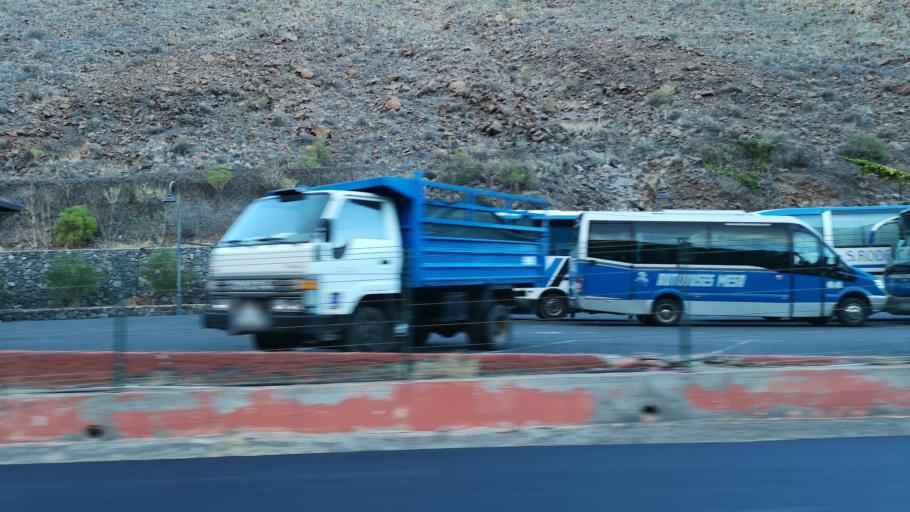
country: ES
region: Canary Islands
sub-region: Provincia de Santa Cruz de Tenerife
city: Alajero
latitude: 28.0347
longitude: -17.2059
